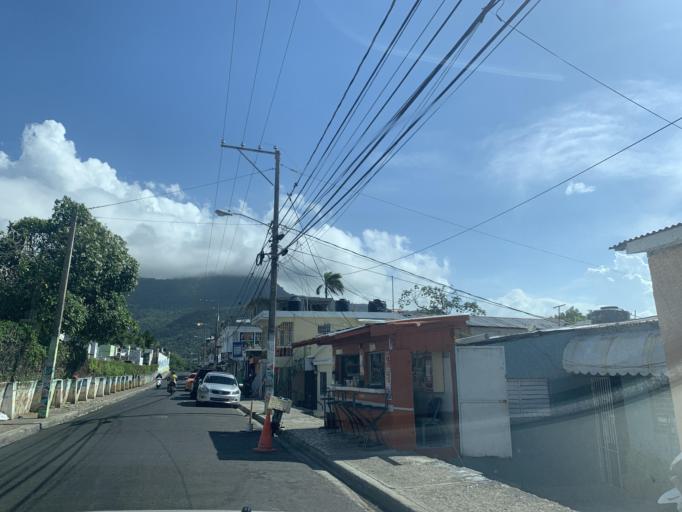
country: DO
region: Puerto Plata
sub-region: Puerto Plata
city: Puerto Plata
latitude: 19.7952
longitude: -70.6936
